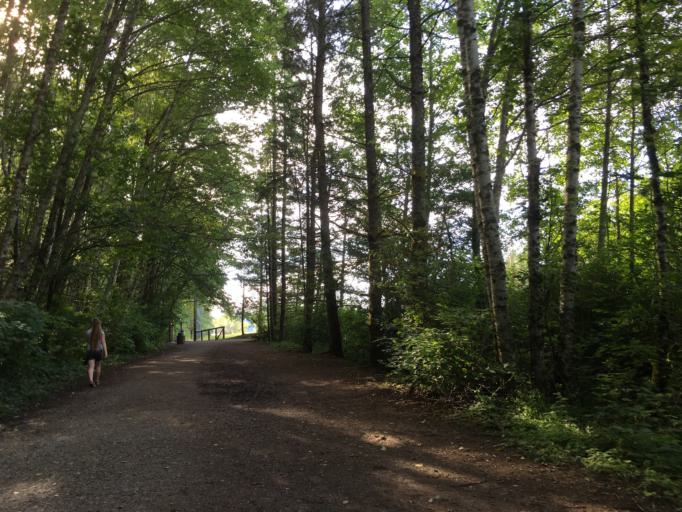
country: US
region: Washington
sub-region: Whatcom County
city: Geneva
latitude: 48.6977
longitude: -122.4426
